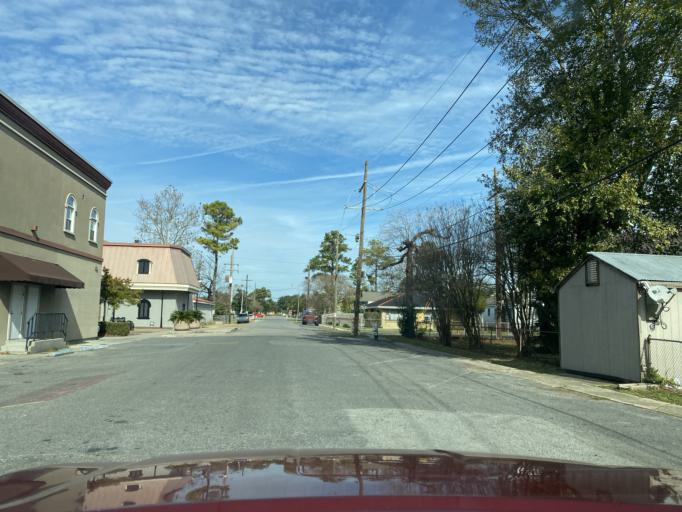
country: US
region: Louisiana
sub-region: Jefferson Parish
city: Kenner
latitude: 29.9740
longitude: -90.2476
